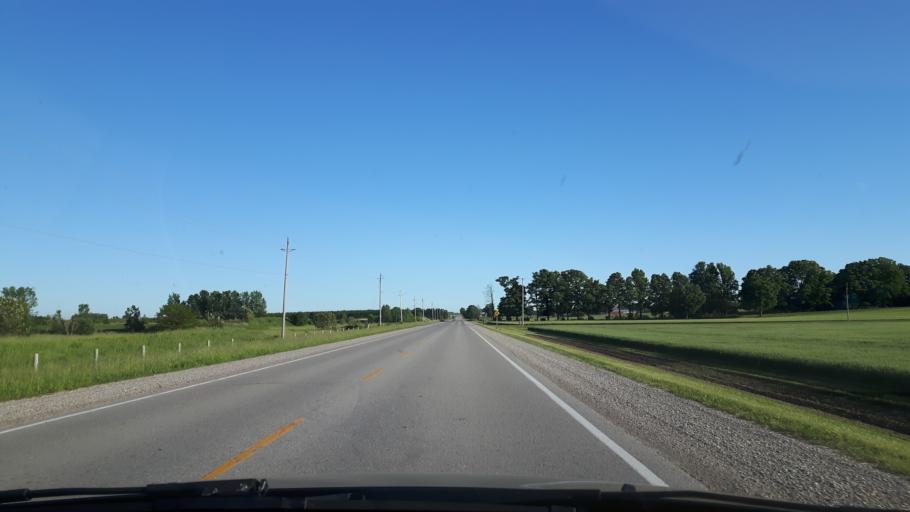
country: CA
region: Ontario
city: Bluewater
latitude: 43.6087
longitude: -81.6022
